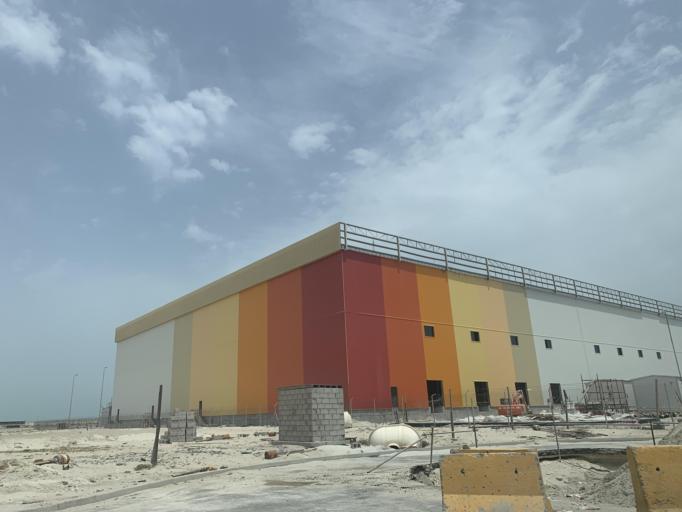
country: BH
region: Muharraq
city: Al Hadd
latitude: 26.2232
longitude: 50.6840
